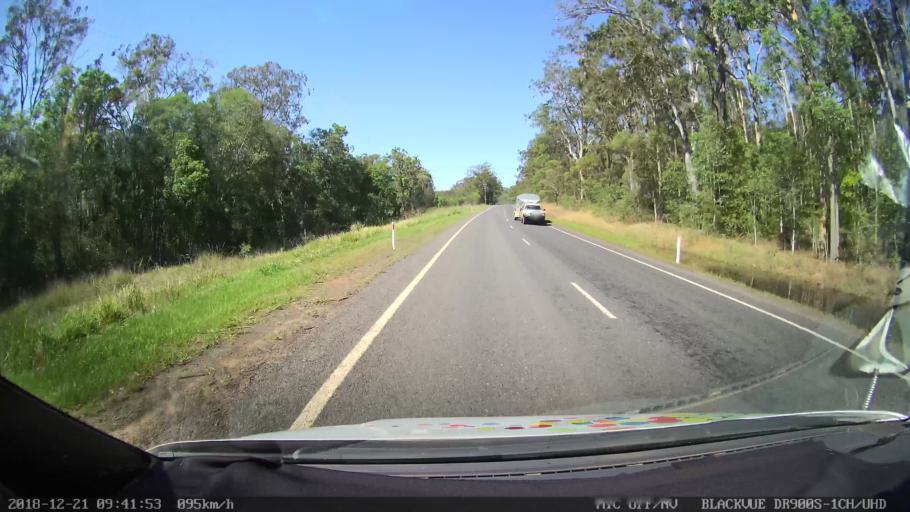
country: AU
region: New South Wales
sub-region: Clarence Valley
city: Grafton
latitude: -29.5900
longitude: 152.9528
